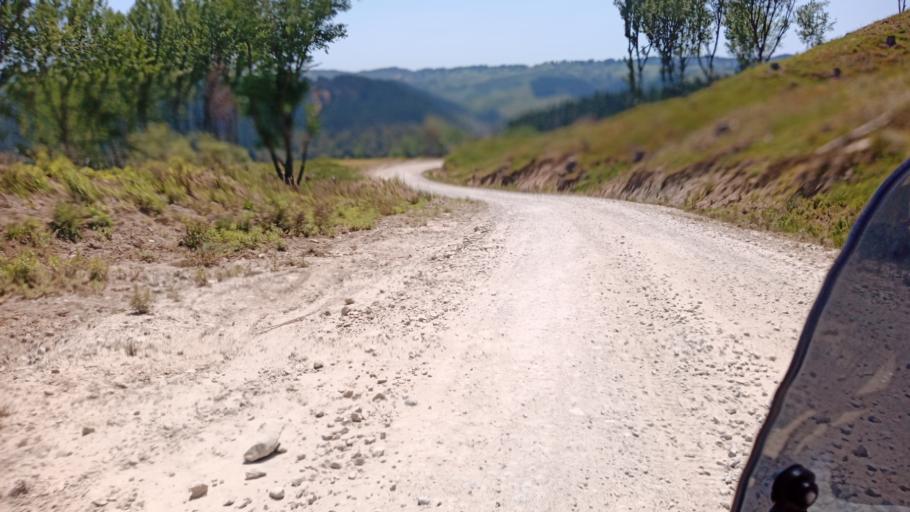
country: NZ
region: Gisborne
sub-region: Gisborne District
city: Gisborne
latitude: -38.2897
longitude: 178.0077
